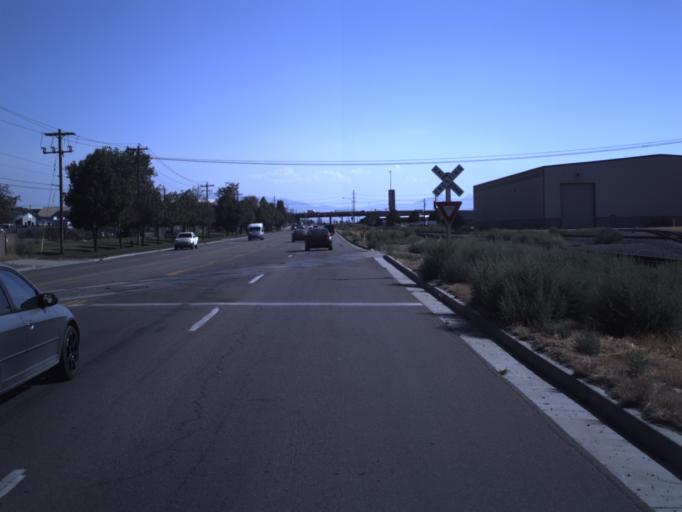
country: US
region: Utah
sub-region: Utah County
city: Lindon
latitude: 40.3370
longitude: -111.7394
